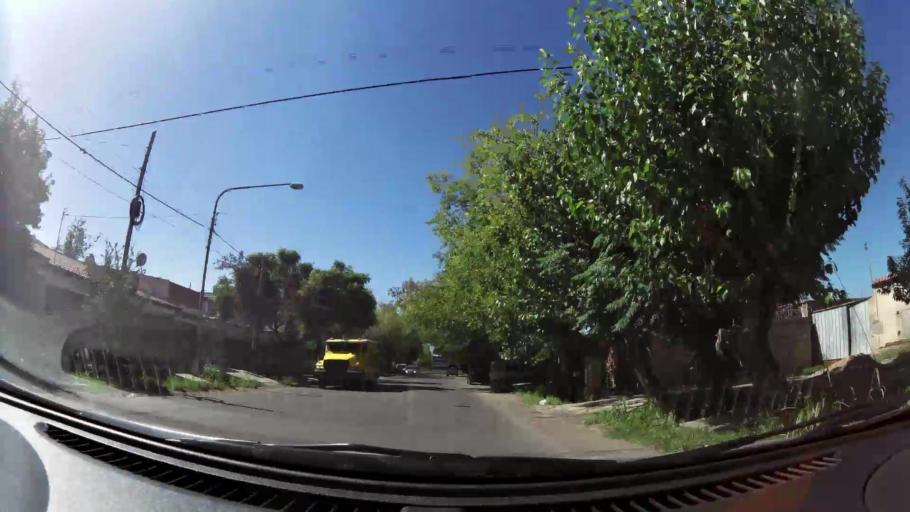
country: AR
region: Mendoza
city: Villa Nueva
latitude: -32.8888
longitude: -68.7826
